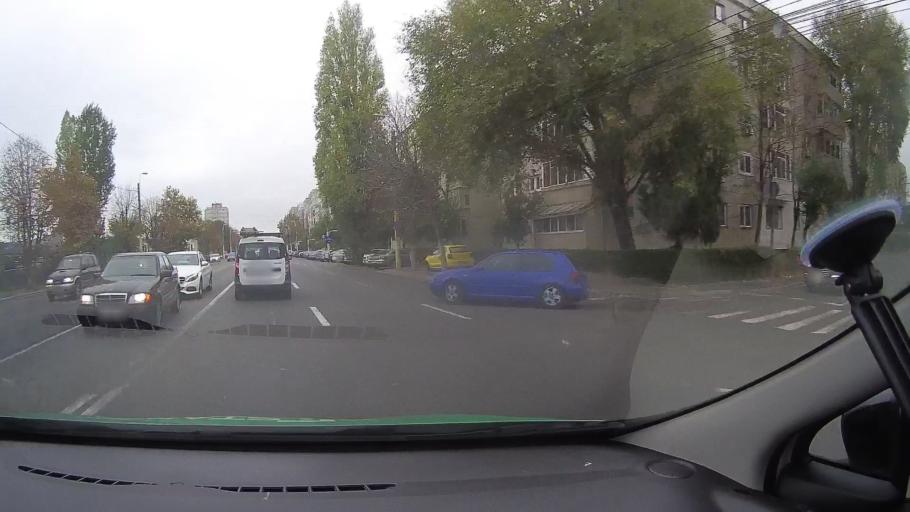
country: RO
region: Constanta
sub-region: Municipiul Constanta
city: Constanta
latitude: 44.1712
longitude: 28.6152
